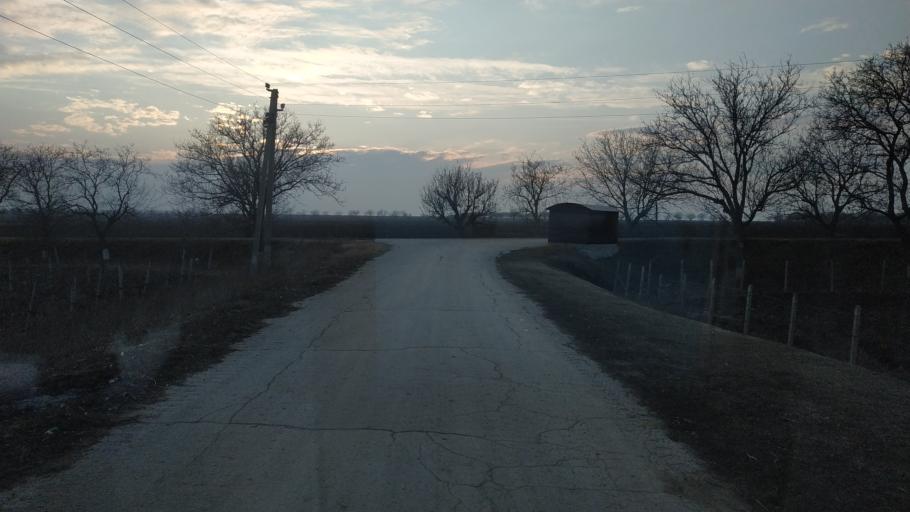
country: MD
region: Hincesti
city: Dancu
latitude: 46.7043
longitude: 28.3398
